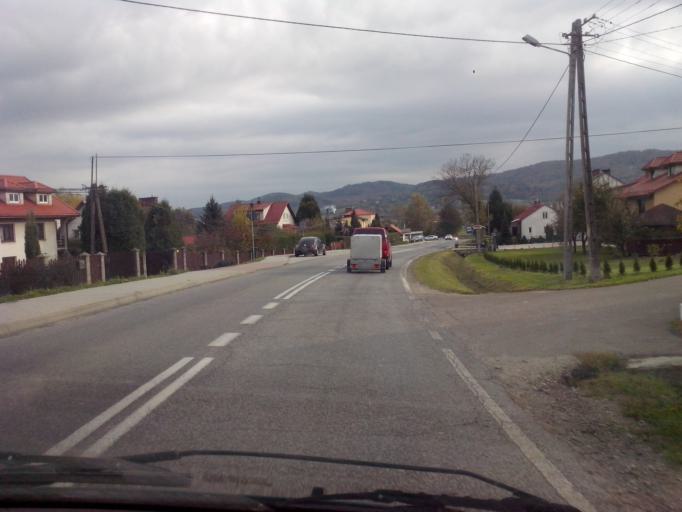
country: PL
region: Subcarpathian Voivodeship
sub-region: Powiat strzyzowski
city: Wisniowa
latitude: 49.8712
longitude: 21.6595
